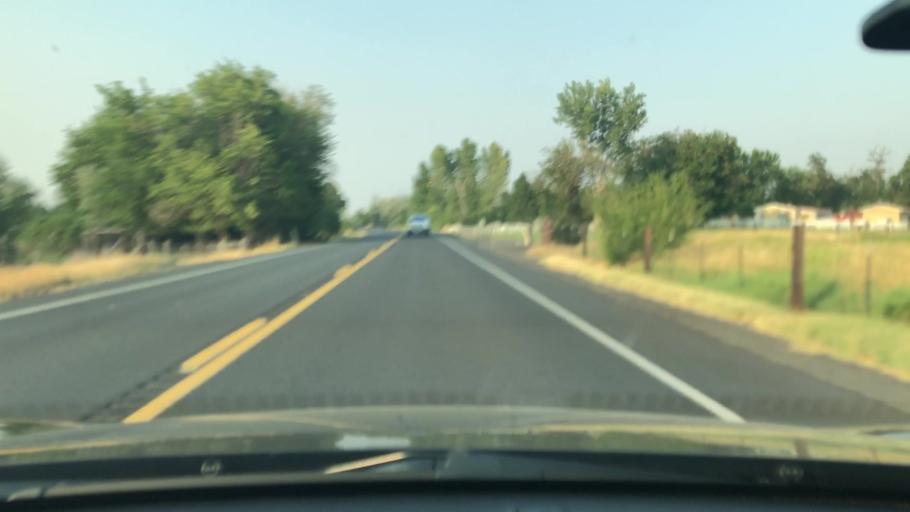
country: US
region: Oregon
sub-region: Umatilla County
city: Hermiston
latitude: 45.8876
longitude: -119.1904
